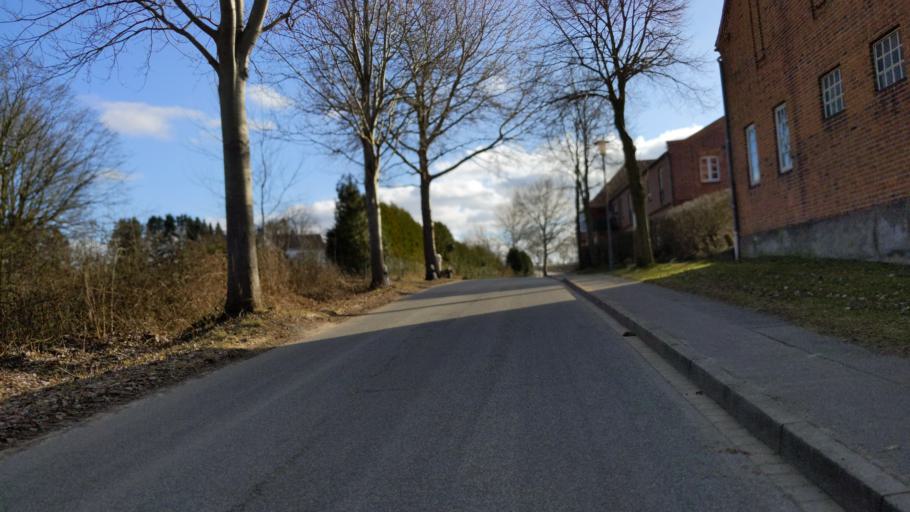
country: DE
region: Schleswig-Holstein
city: Scharbeutz
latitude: 54.0110
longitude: 10.7536
